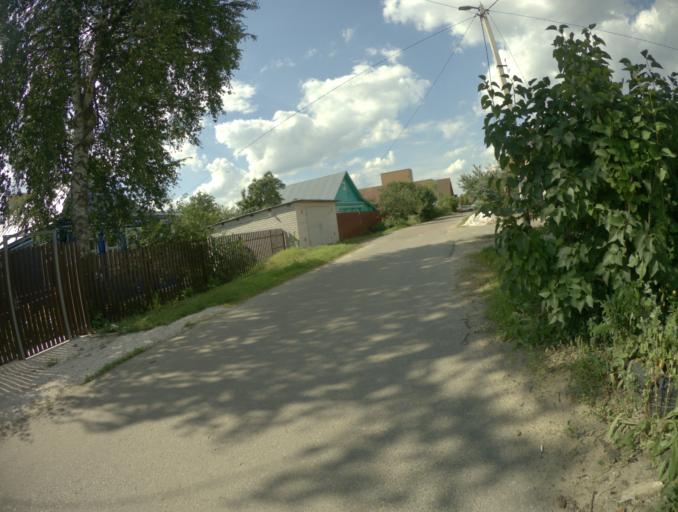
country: RU
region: Vladimir
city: Vladimir
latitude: 56.1083
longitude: 40.3625
